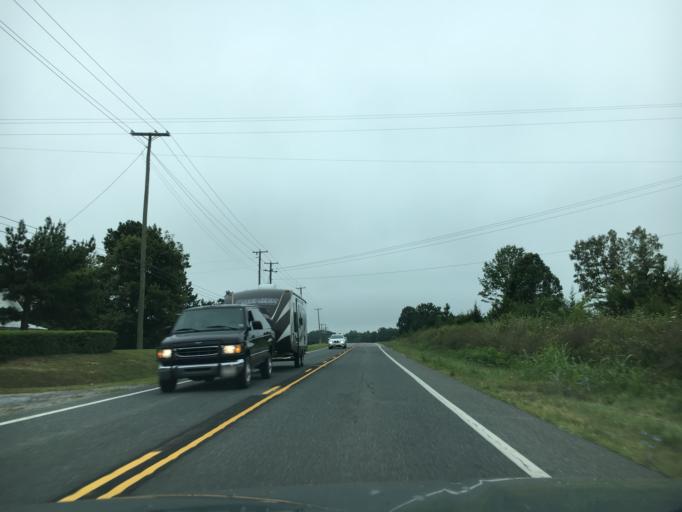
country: US
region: Virginia
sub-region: Campbell County
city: Brookneal
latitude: 37.0821
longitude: -78.9864
